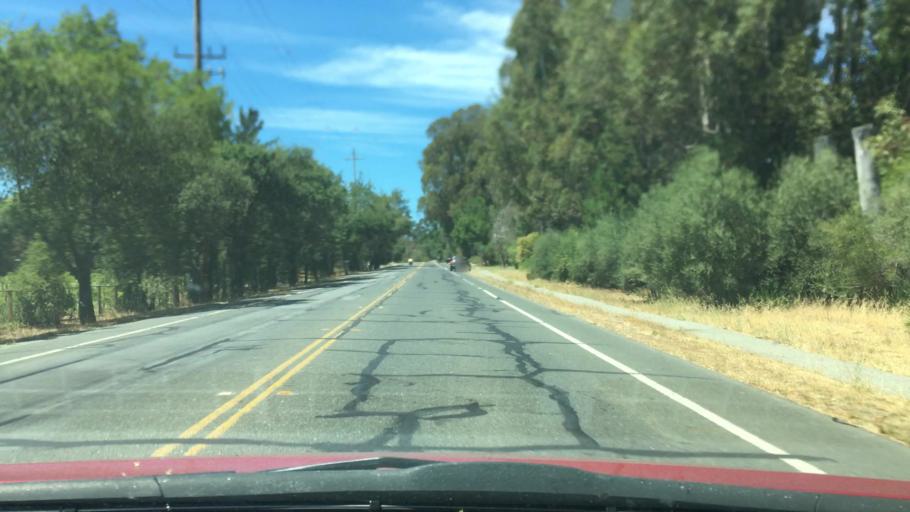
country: US
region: California
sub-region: San Mateo County
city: Woodside
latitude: 37.4411
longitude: -122.2657
